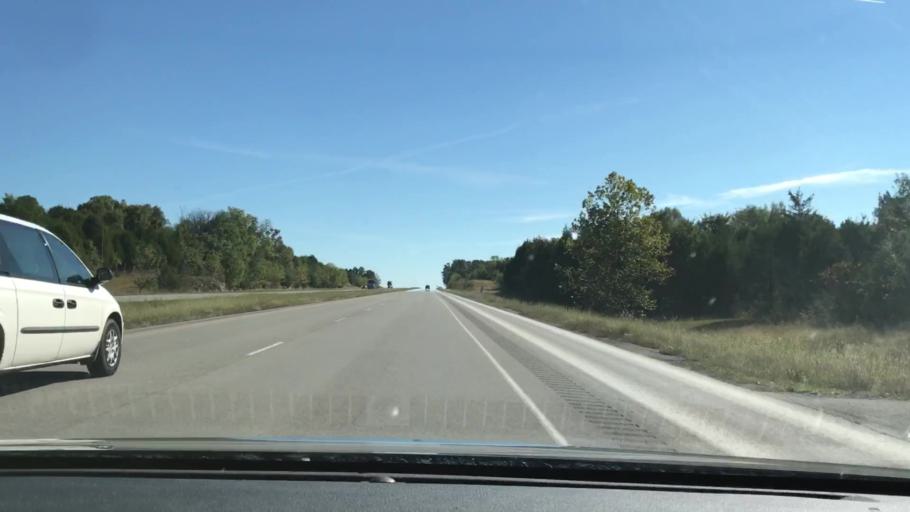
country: US
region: Kentucky
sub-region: Todd County
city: Elkton
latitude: 36.8474
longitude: -87.3199
